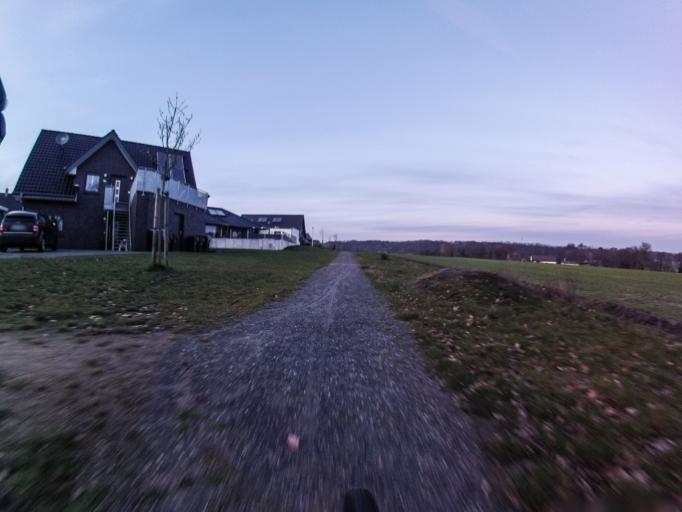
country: DE
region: North Rhine-Westphalia
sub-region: Regierungsbezirk Munster
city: Tecklenburg
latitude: 52.2629
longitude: 7.7951
